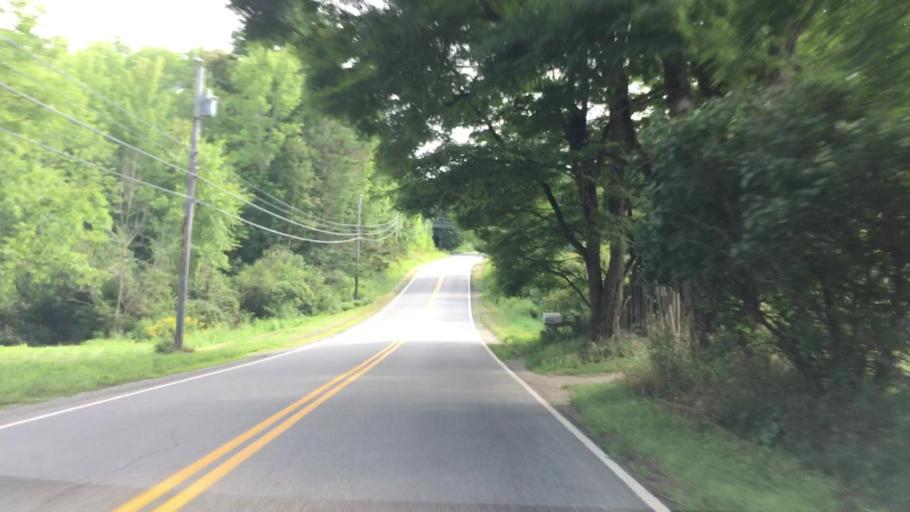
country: US
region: Maine
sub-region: Waldo County
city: Belfast
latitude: 44.4041
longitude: -69.0309
